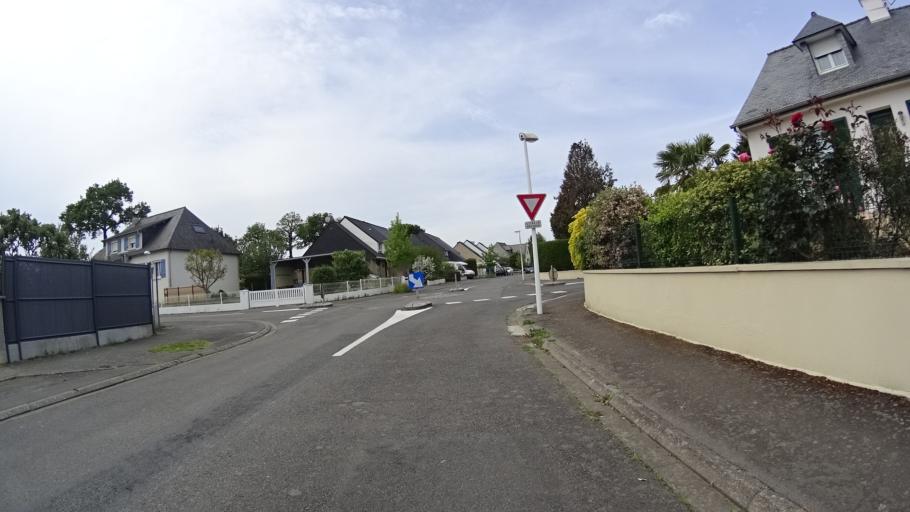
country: FR
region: Brittany
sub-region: Departement d'Ille-et-Vilaine
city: La Meziere
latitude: 48.2173
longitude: -1.7575
